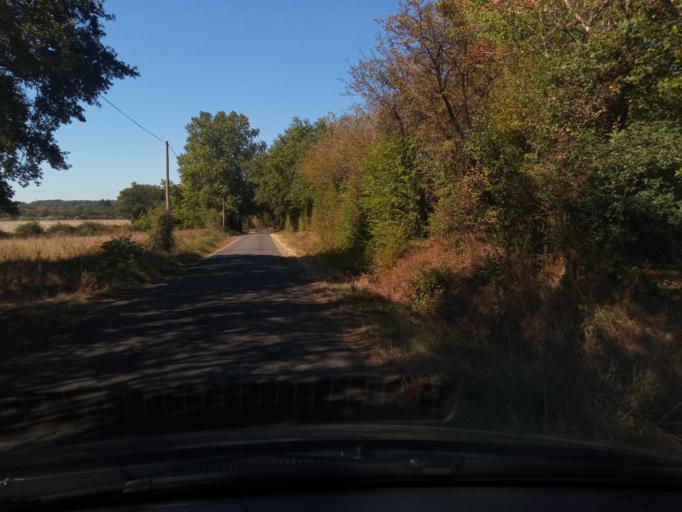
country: FR
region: Poitou-Charentes
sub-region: Departement de la Vienne
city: Montmorillon
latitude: 46.4825
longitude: 0.8492
